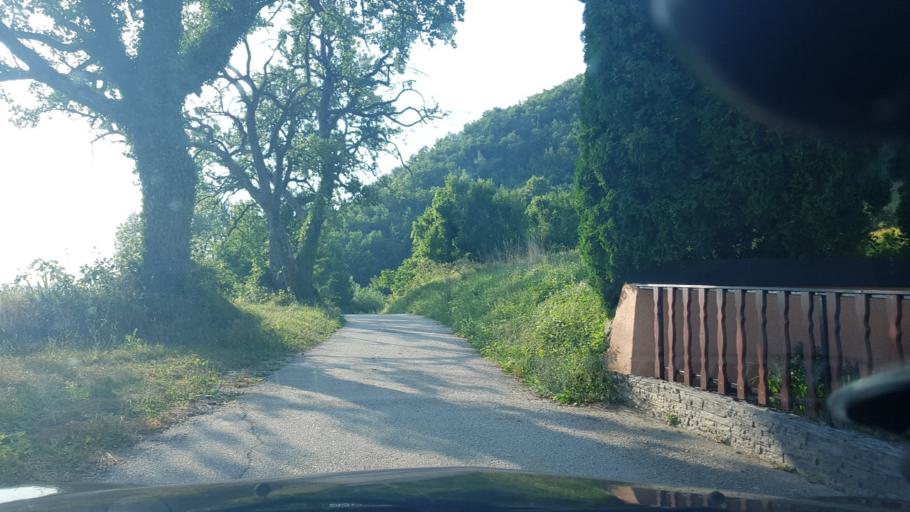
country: HR
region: Krapinsko-Zagorska
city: Radoboj
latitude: 46.1755
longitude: 15.9013
